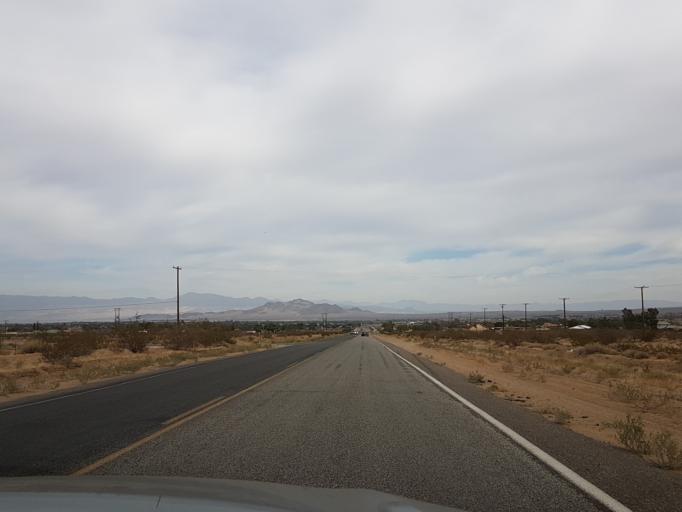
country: US
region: California
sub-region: Kern County
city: Ridgecrest
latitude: 35.5896
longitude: -117.6971
